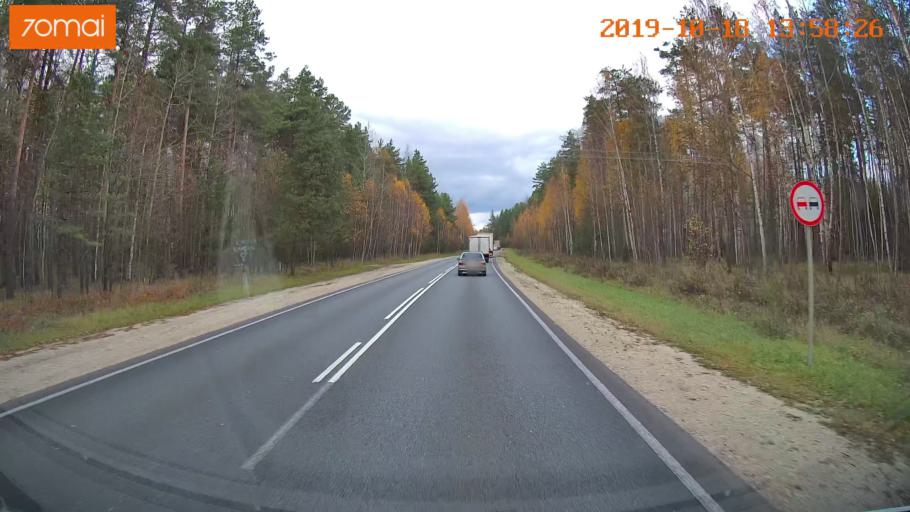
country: RU
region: Rjazan
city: Spas-Klepiki
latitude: 55.0849
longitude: 40.0543
